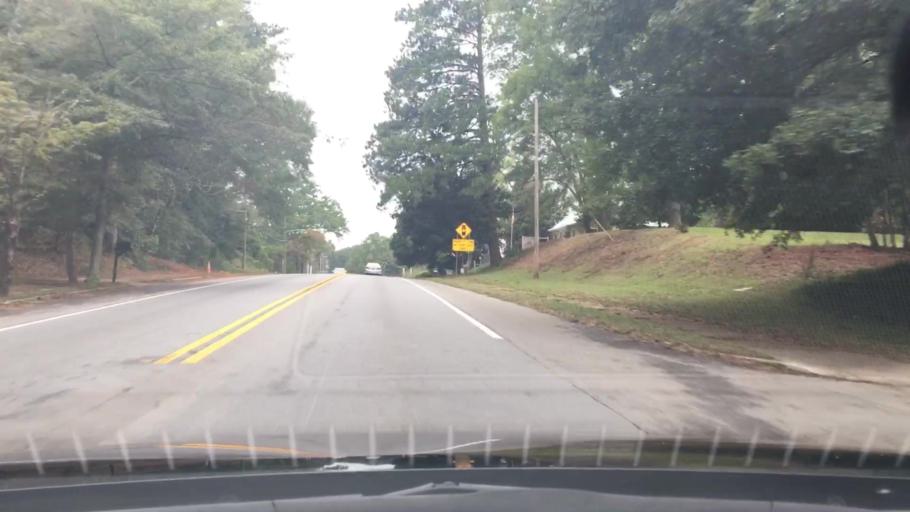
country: US
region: Georgia
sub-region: Coweta County
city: Senoia
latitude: 33.2965
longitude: -84.5509
